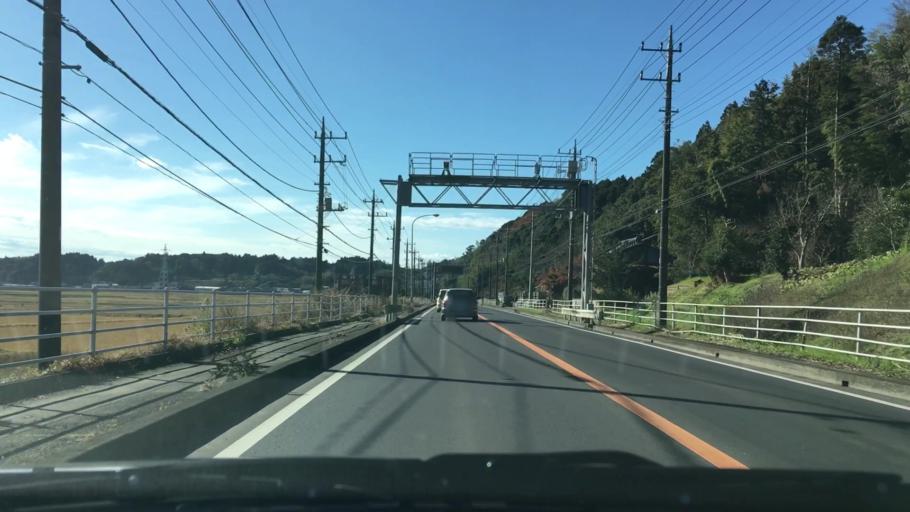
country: JP
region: Chiba
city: Omigawa
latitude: 35.8469
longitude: 140.5767
